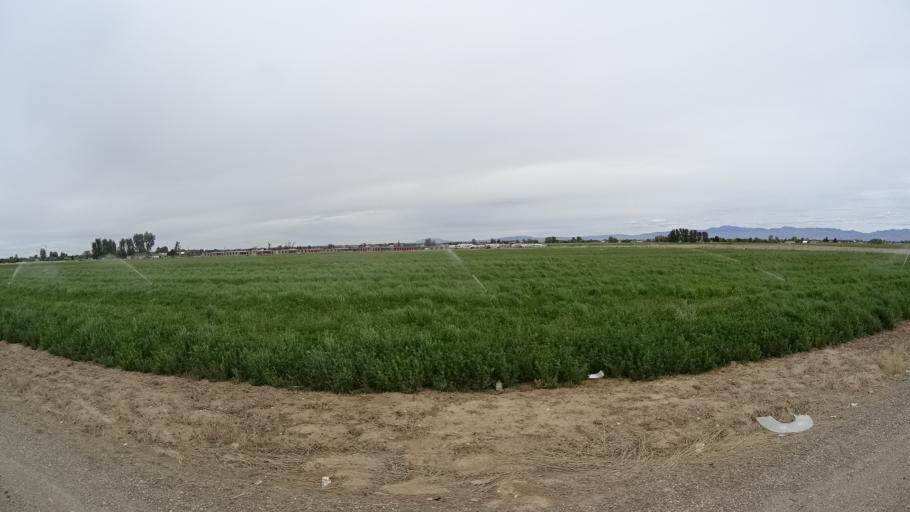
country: US
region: Idaho
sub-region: Ada County
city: Kuna
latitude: 43.4878
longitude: -116.3905
